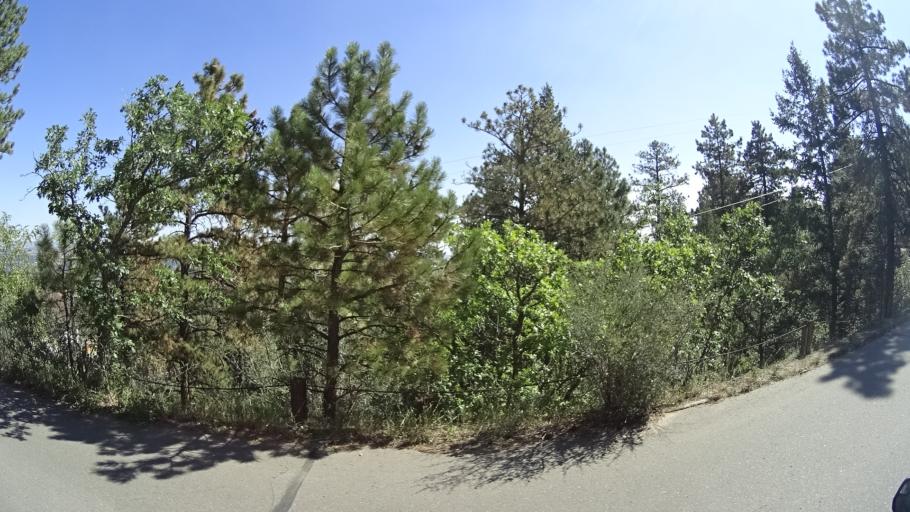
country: US
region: Colorado
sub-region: El Paso County
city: Colorado Springs
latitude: 38.8100
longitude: -104.8791
